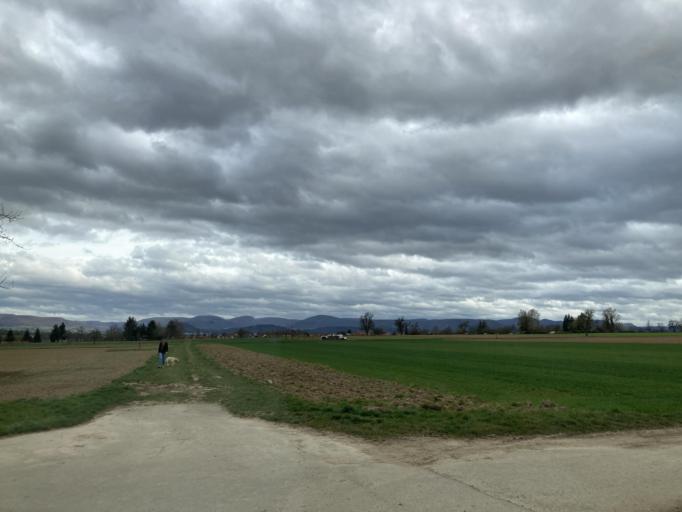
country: DE
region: Baden-Wuerttemberg
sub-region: Tuebingen Region
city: Sickenhausen
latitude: 48.5306
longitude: 9.1714
